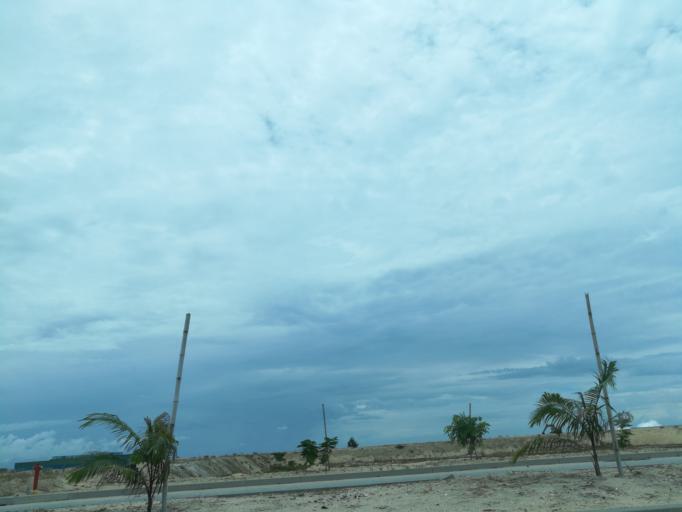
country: NG
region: Lagos
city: Ikoyi
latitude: 6.4112
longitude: 3.4225
